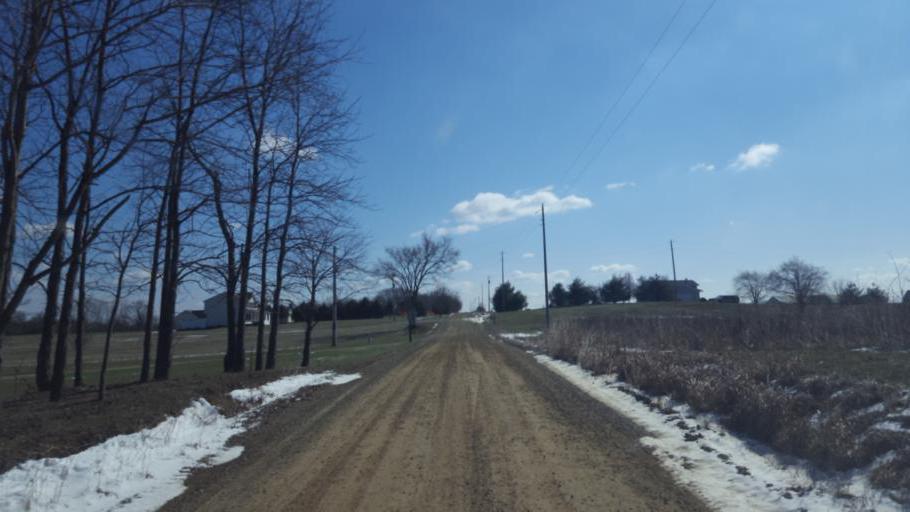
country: US
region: Ohio
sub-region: Licking County
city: Utica
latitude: 40.2872
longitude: -82.4814
